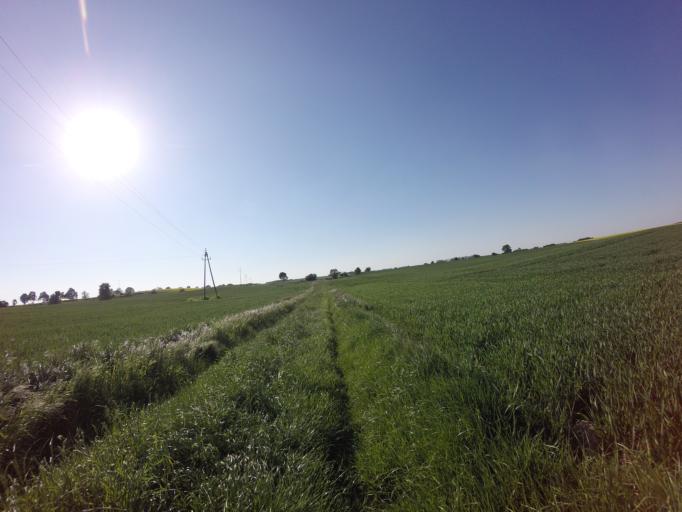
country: PL
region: West Pomeranian Voivodeship
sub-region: Powiat choszczenski
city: Choszczno
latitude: 53.1354
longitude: 15.3713
